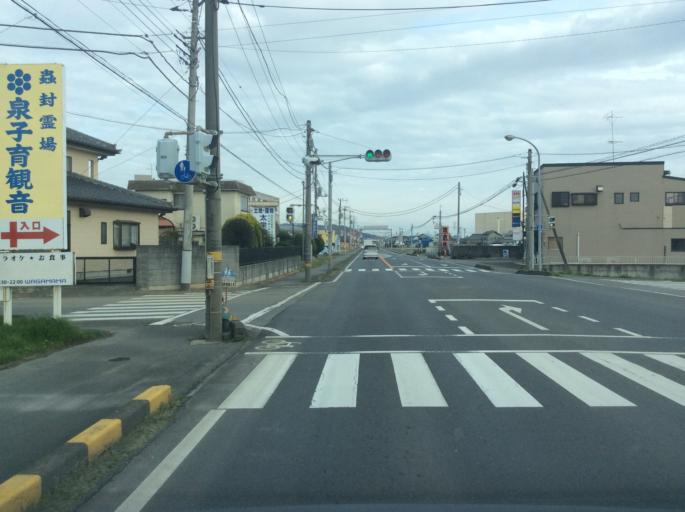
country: JP
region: Ibaraki
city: Tsukuba
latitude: 36.1770
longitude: 140.0850
